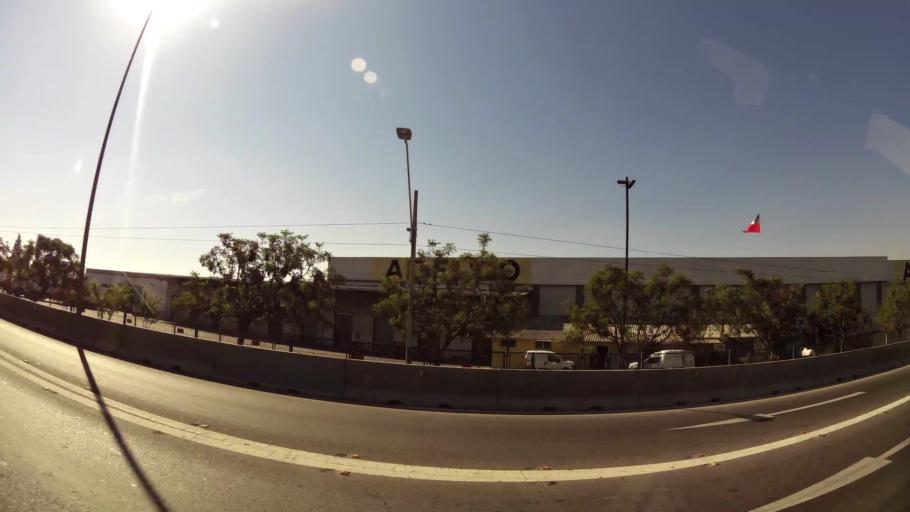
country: CL
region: Santiago Metropolitan
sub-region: Provincia de Santiago
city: La Pintana
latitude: -33.5426
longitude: -70.6276
